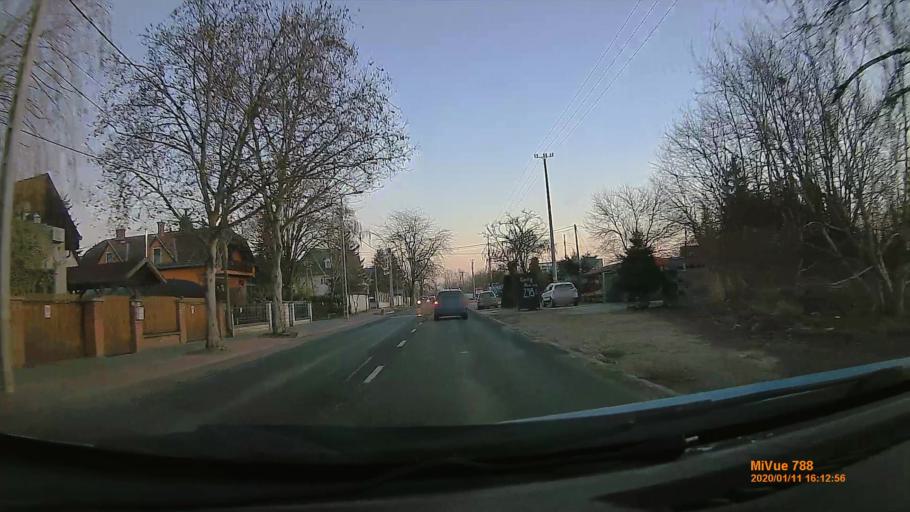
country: HU
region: Budapest
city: Budapest XVI. keruelet
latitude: 47.5385
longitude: 19.1752
